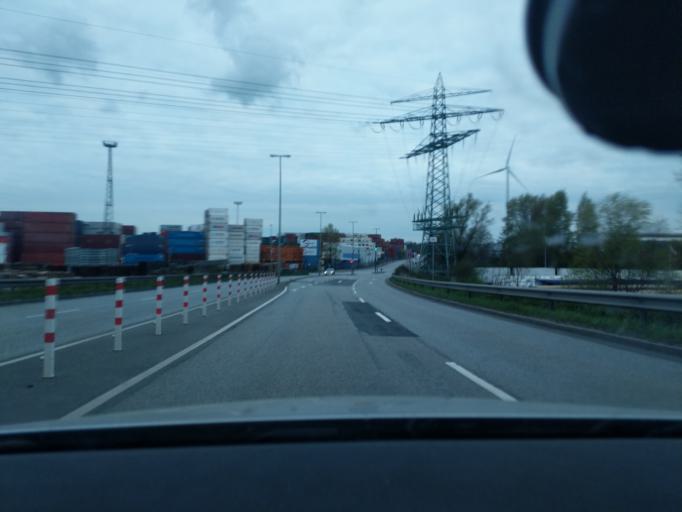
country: DE
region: Hamburg
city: Altona
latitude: 53.5129
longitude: 9.9021
